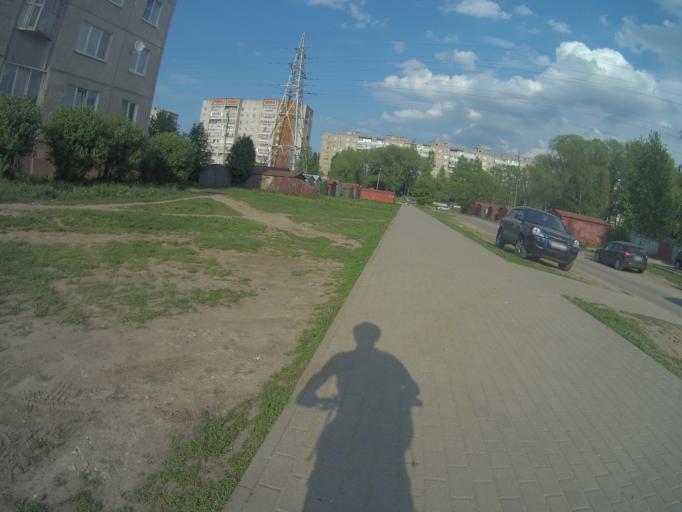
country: RU
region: Vladimir
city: Kommunar
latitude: 56.1679
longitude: 40.4533
